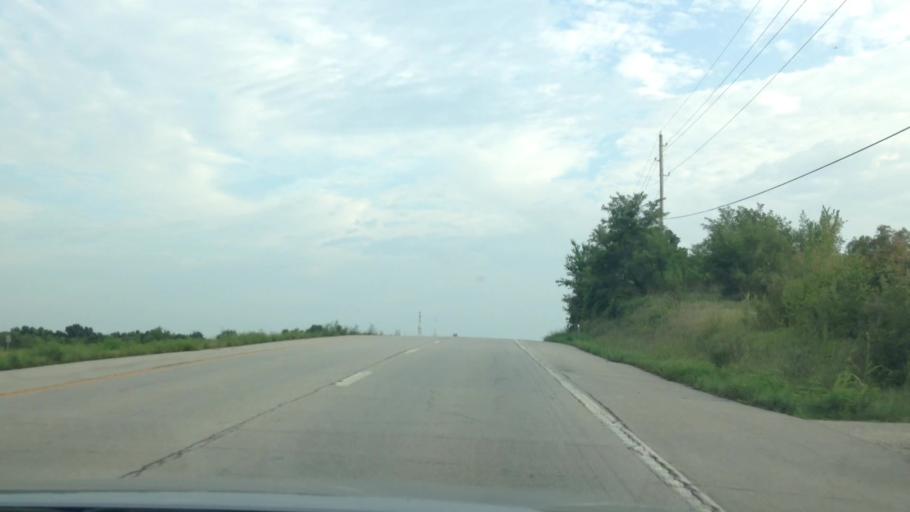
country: US
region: Missouri
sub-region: Clay County
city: Smithville
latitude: 39.3491
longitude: -94.5838
